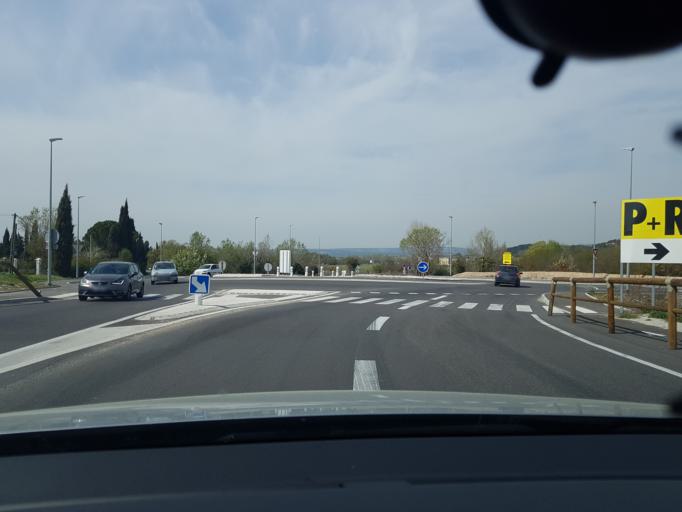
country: FR
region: Provence-Alpes-Cote d'Azur
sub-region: Departement des Bouches-du-Rhone
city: Bouc-Bel-Air
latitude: 43.4725
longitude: 5.3998
